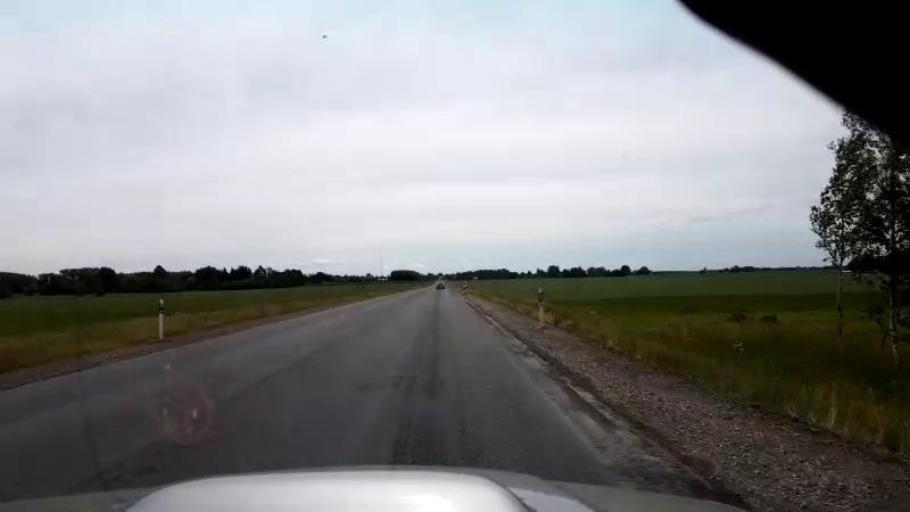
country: LV
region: Bauskas Rajons
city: Bauska
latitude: 56.3741
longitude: 24.2683
